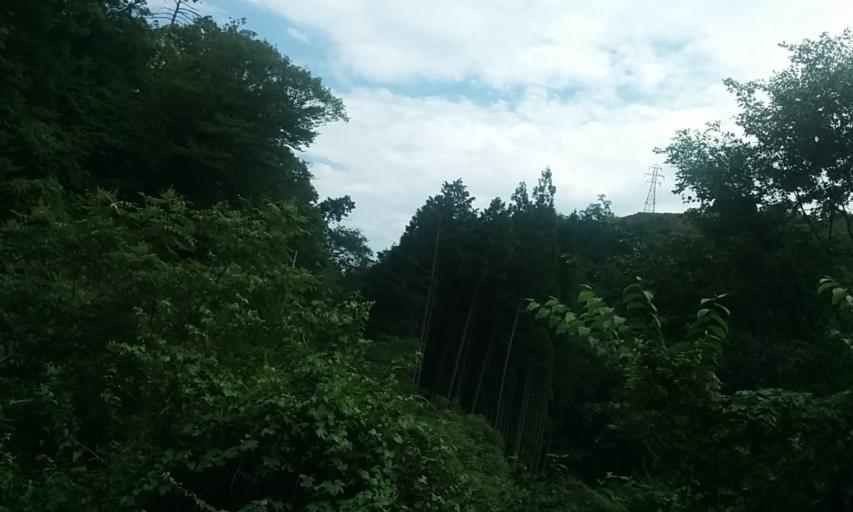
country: JP
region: Kyoto
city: Maizuru
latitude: 35.3534
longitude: 135.3449
